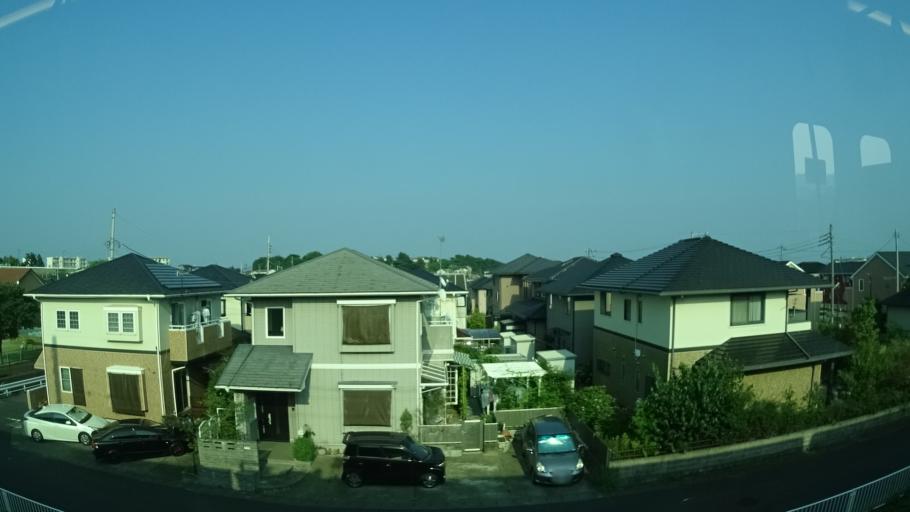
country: JP
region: Ibaraki
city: Hitachi
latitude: 36.6292
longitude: 140.6769
